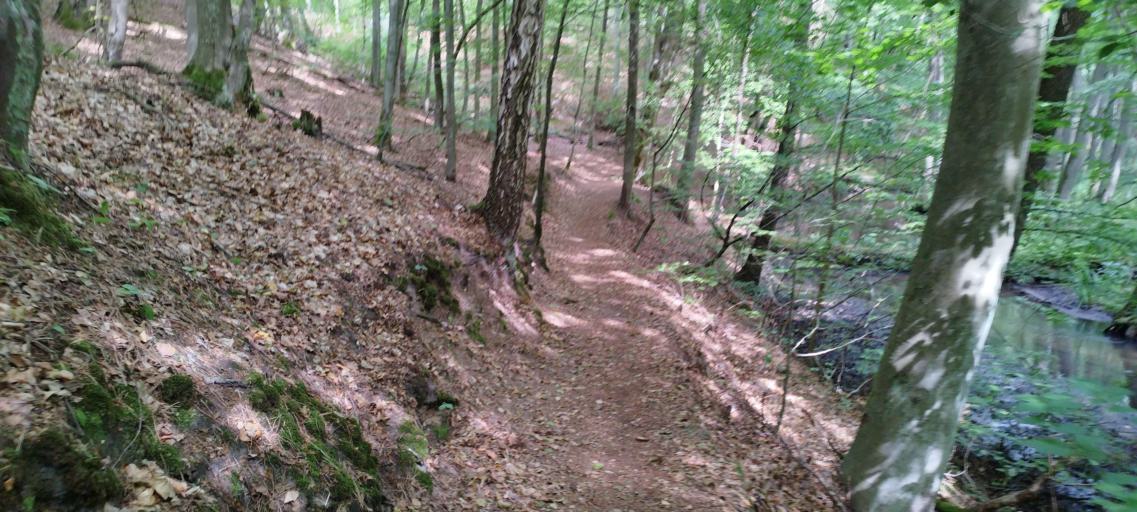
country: DE
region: Brandenburg
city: Mixdorf
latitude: 52.1288
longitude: 14.4654
